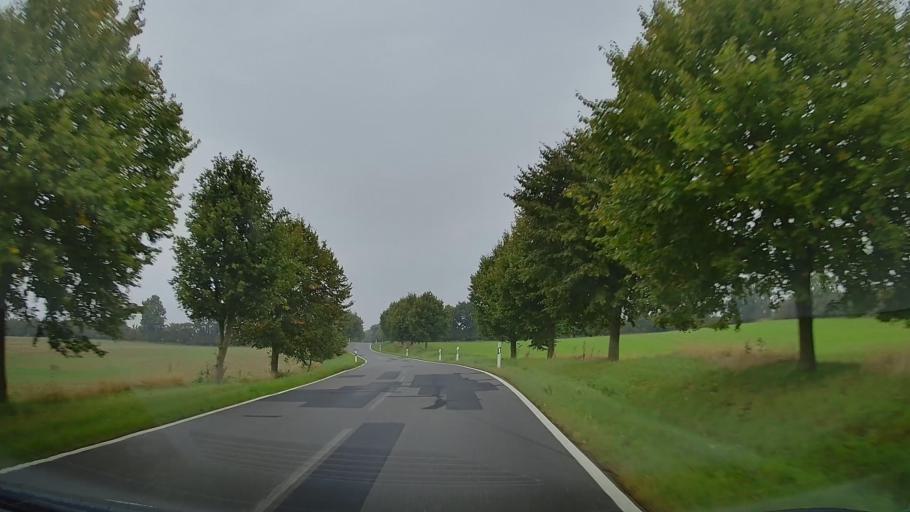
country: DE
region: Mecklenburg-Vorpommern
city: Kalkhorst
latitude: 53.9783
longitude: 11.0483
